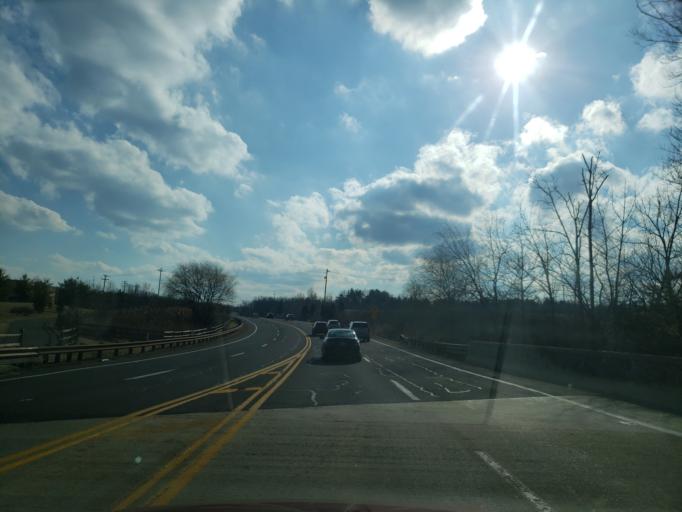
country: US
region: Pennsylvania
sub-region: Montgomery County
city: Montgomeryville
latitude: 40.2291
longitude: -75.2415
